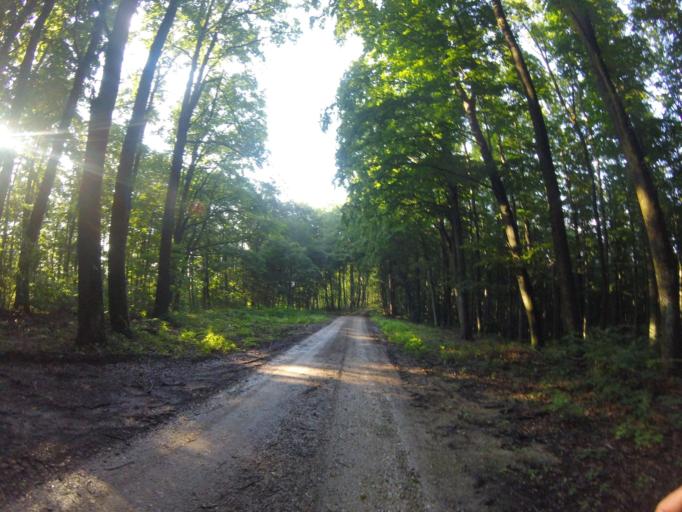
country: HU
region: Zala
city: Letenye
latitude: 46.5187
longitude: 16.7159
